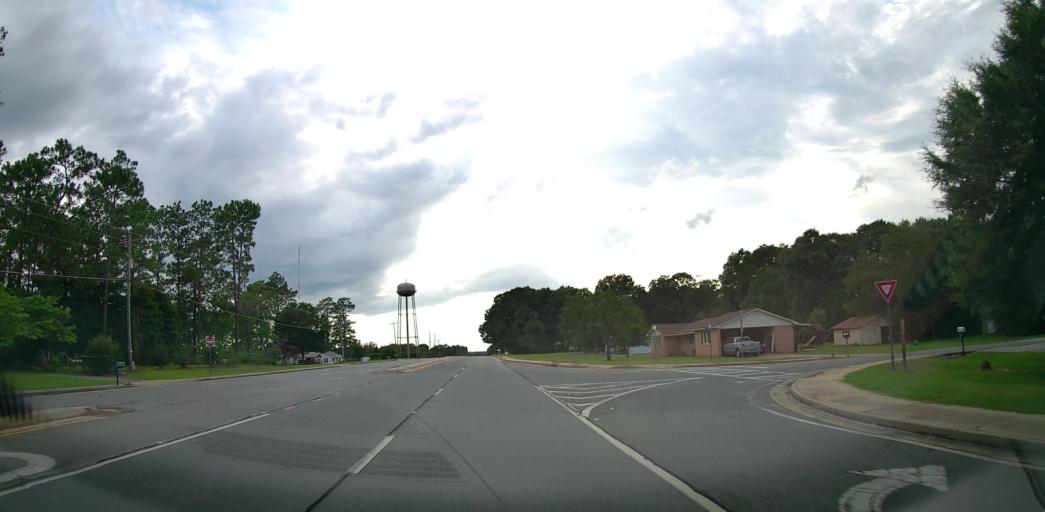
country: US
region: Georgia
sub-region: Pulaski County
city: Hawkinsville
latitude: 32.2815
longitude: -83.4371
